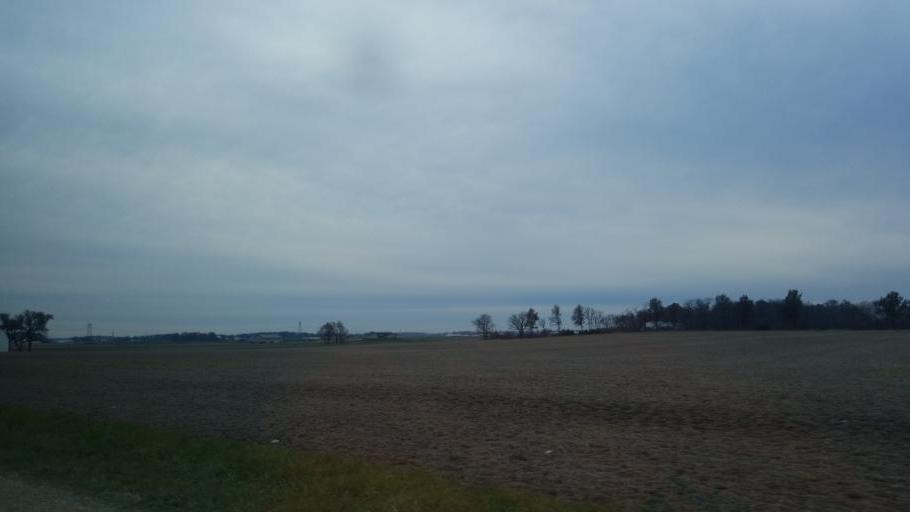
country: US
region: Indiana
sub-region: Adams County
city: Berne
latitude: 40.6761
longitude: -84.8790
